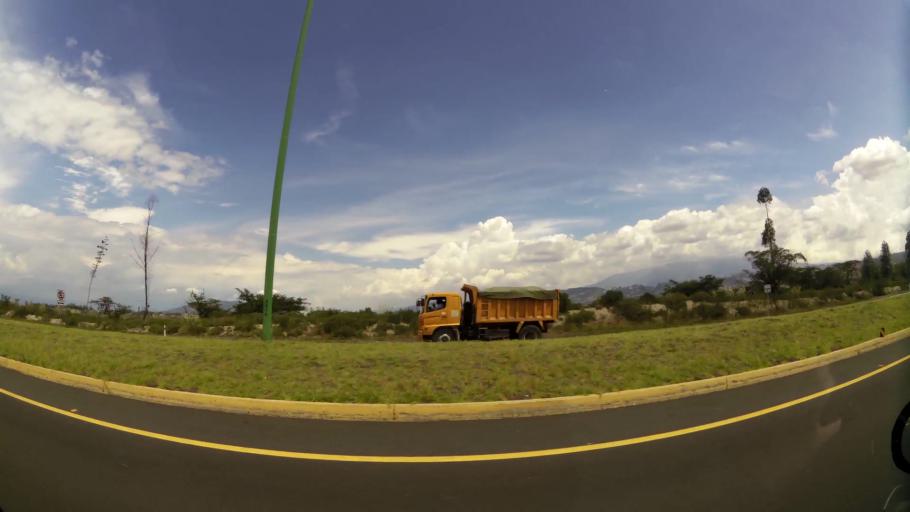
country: EC
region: Pichincha
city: Quito
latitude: -0.1263
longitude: -78.3644
